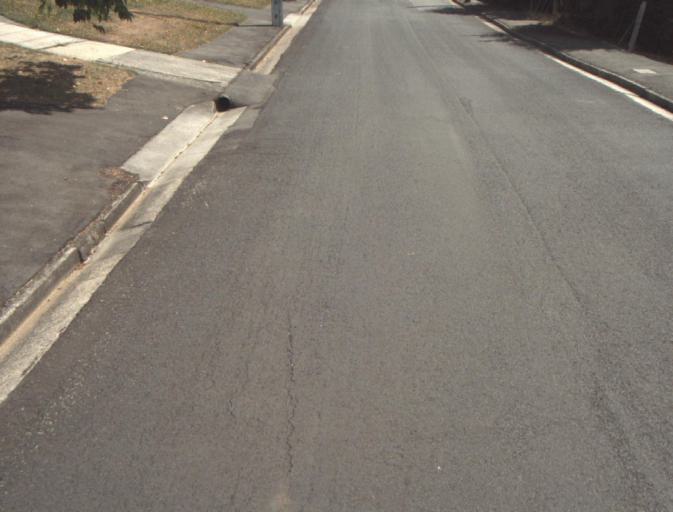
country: AU
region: Tasmania
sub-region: Launceston
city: Newnham
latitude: -41.4121
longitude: 147.1517
